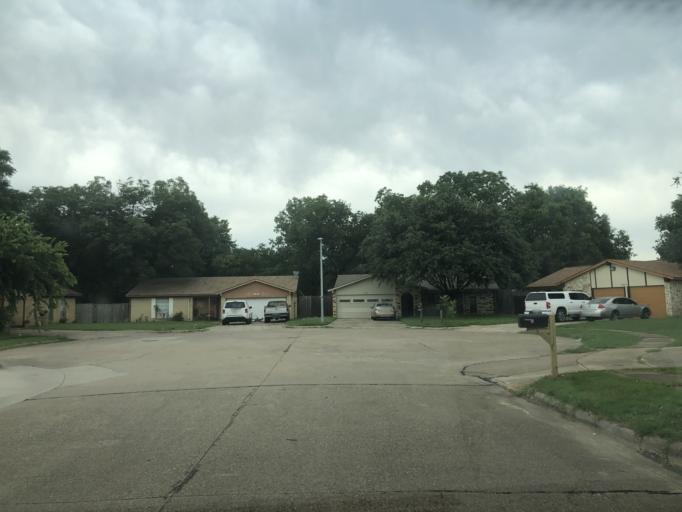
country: US
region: Texas
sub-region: Dallas County
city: Irving
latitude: 32.7836
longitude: -96.9680
